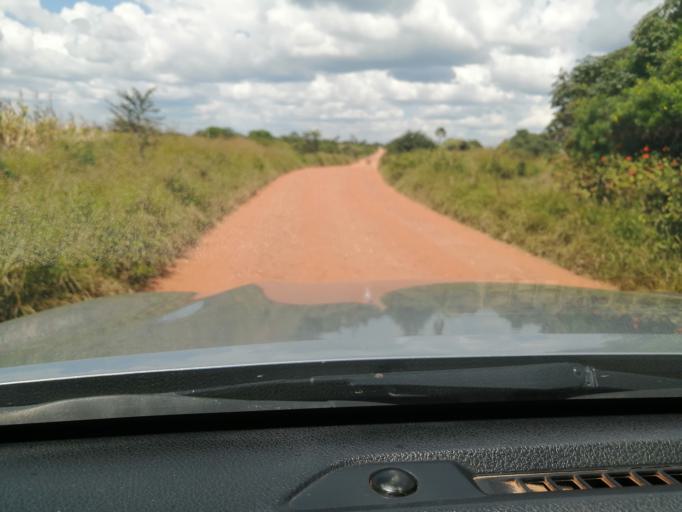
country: ZM
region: Lusaka
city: Lusaka
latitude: -15.1936
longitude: 27.9734
